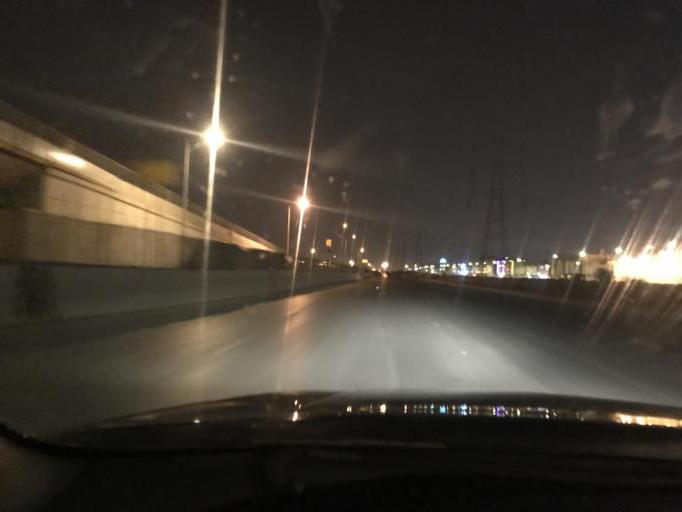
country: SA
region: Ar Riyad
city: Riyadh
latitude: 24.8023
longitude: 46.6988
